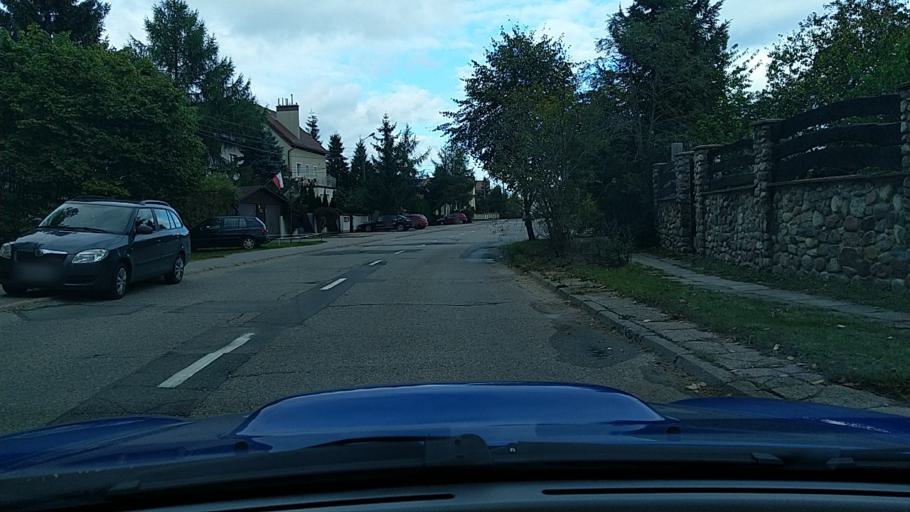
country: PL
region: Warmian-Masurian Voivodeship
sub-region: Olsztyn
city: Kortowo
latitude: 53.7649
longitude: 20.4165
